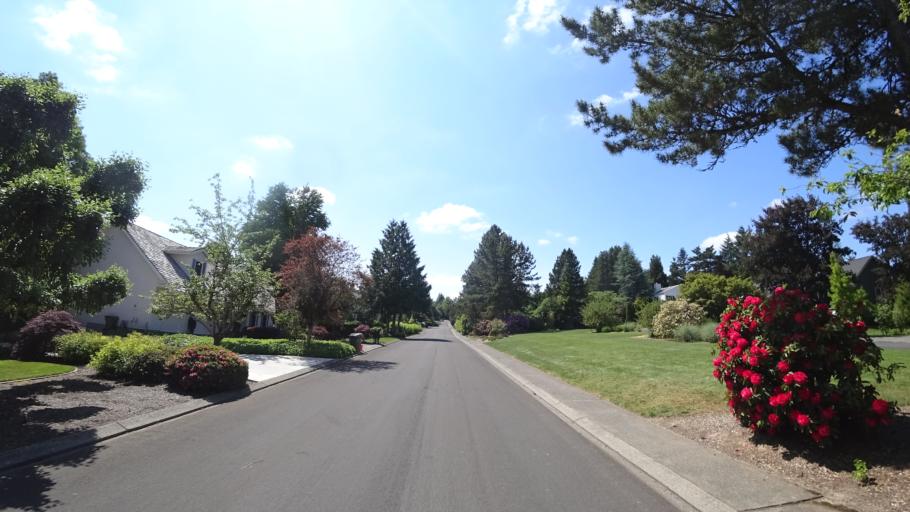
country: US
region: Oregon
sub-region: Clackamas County
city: Lake Oswego
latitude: 45.4285
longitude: -122.6870
